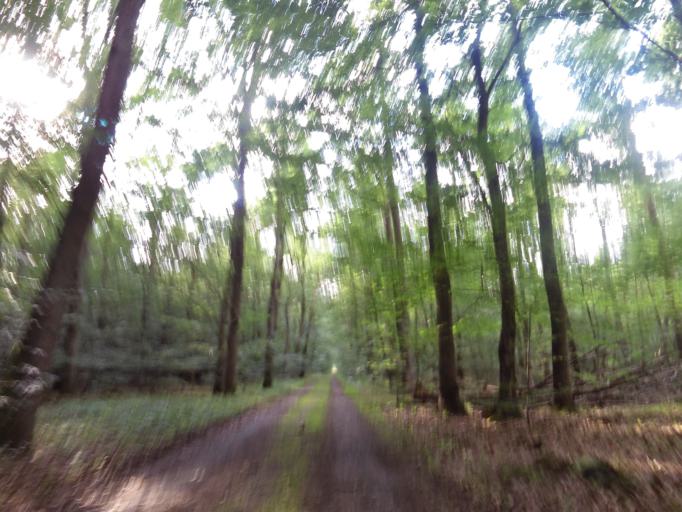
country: DE
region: Hesse
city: Niederrad
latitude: 50.0426
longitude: 8.6226
